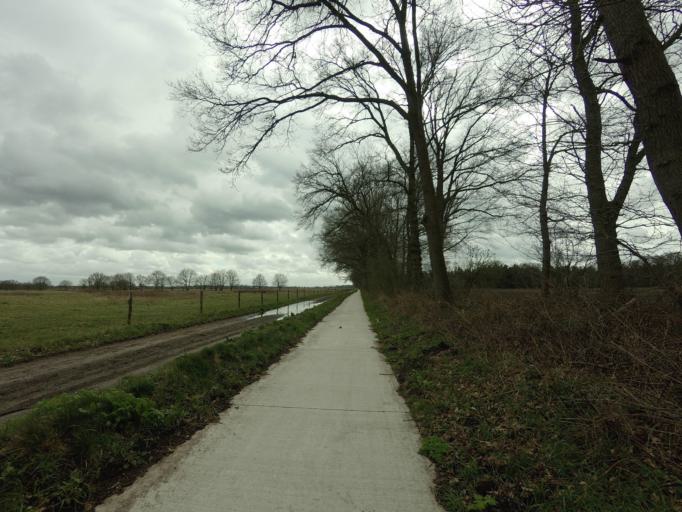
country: NL
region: Gelderland
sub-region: Gemeente Renkum
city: Heelsum
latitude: 52.0057
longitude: 5.7487
